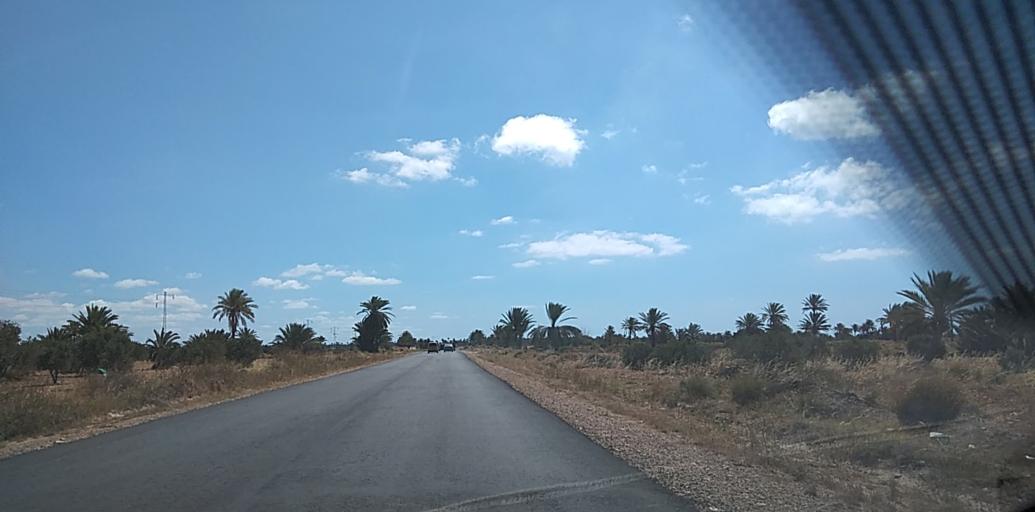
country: TN
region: Safaqis
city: Al Qarmadah
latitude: 34.6578
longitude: 11.0997
